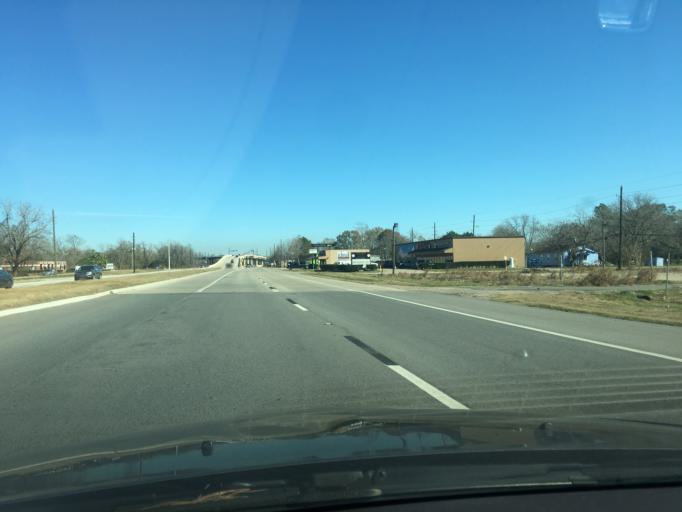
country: US
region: Texas
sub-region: Fort Bend County
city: Richmond
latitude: 29.5900
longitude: -95.7472
